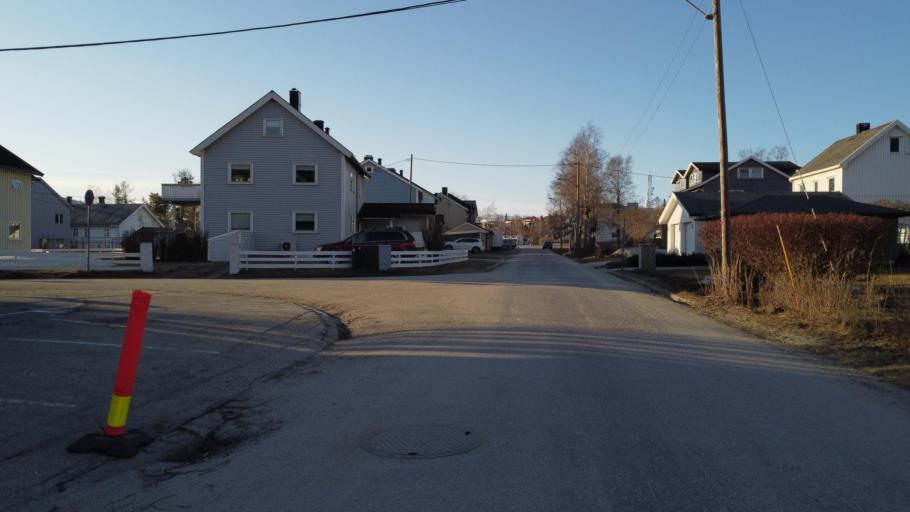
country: NO
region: Nordland
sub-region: Rana
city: Mo i Rana
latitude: 66.3086
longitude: 14.1428
